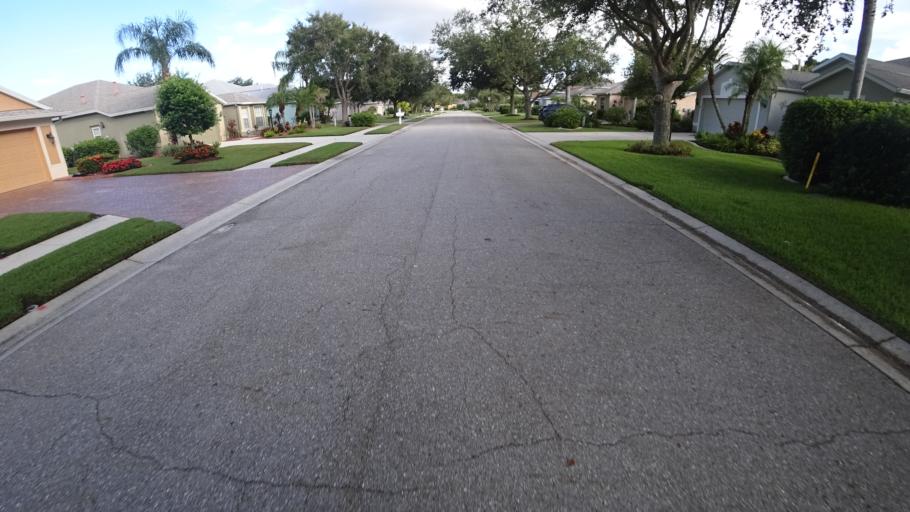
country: US
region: Florida
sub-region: Sarasota County
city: Desoto Lakes
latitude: 27.4230
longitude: -82.4899
